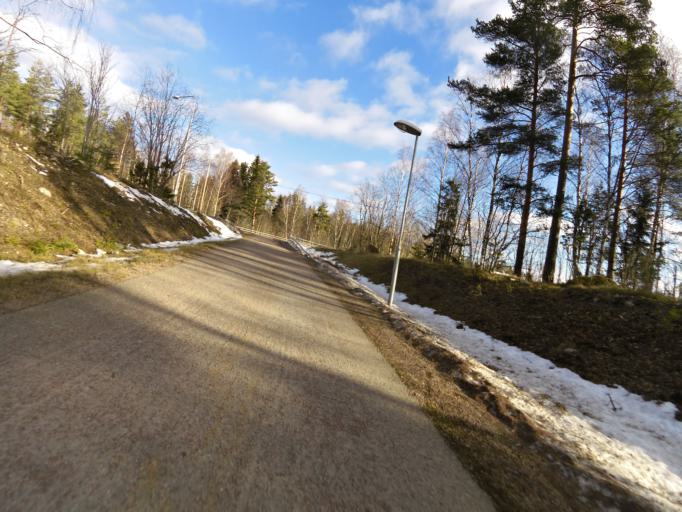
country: SE
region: Uppsala
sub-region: Alvkarleby Kommun
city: Skutskaer
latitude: 60.6501
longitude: 17.3170
